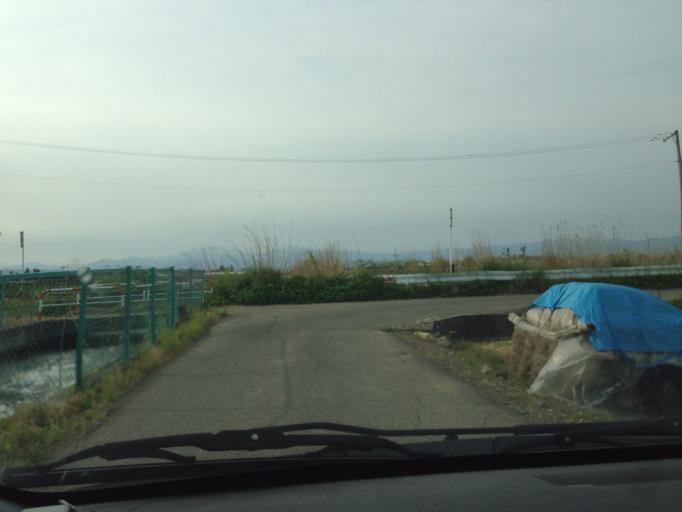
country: JP
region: Fukushima
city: Kitakata
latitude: 37.4626
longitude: 139.8906
